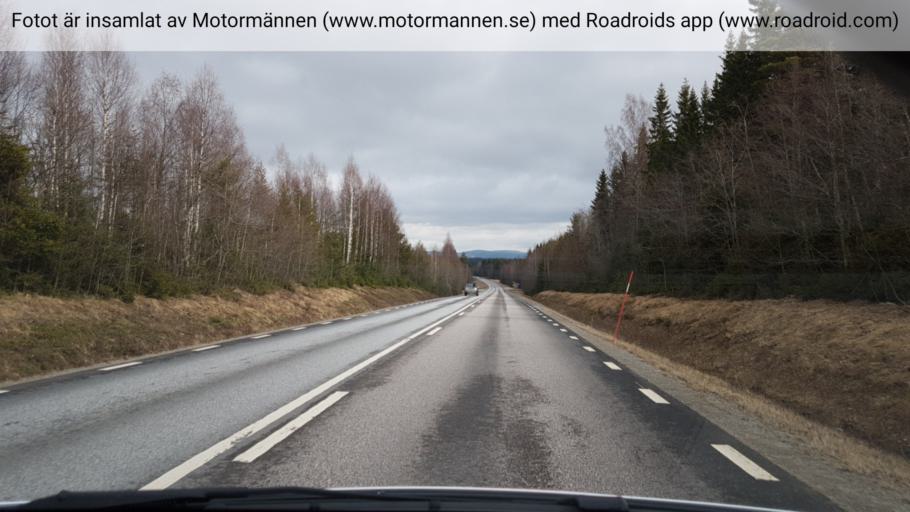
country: SE
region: Vaesterbotten
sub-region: Vannas Kommun
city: Vaennaes
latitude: 63.9235
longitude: 19.6012
